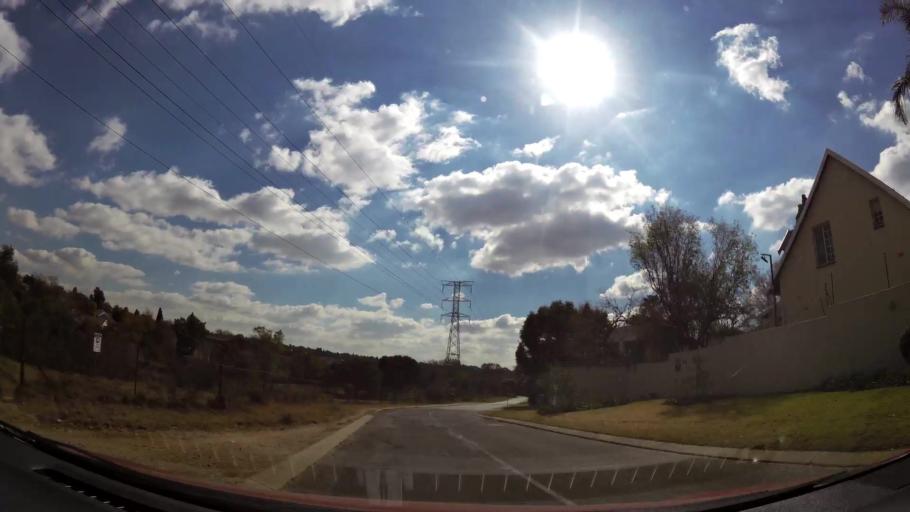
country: ZA
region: Gauteng
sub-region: City of Johannesburg Metropolitan Municipality
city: Roodepoort
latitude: -26.0752
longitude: 27.9653
